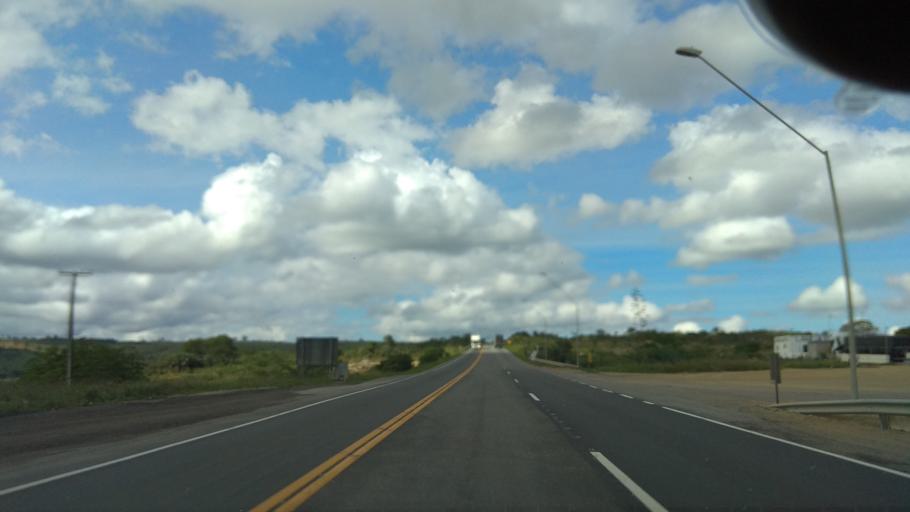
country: BR
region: Bahia
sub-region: Santa Ines
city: Santa Ines
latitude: -13.1046
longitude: -39.9886
